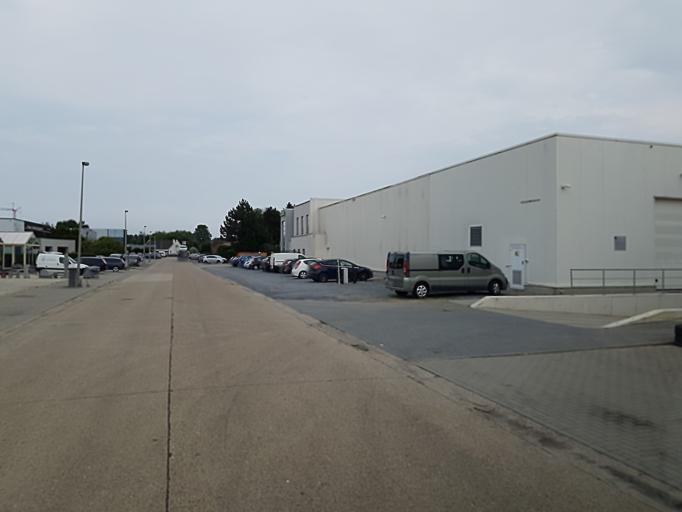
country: BE
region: Flanders
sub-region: Provincie Limburg
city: Halen
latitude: 50.9544
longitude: 5.1134
